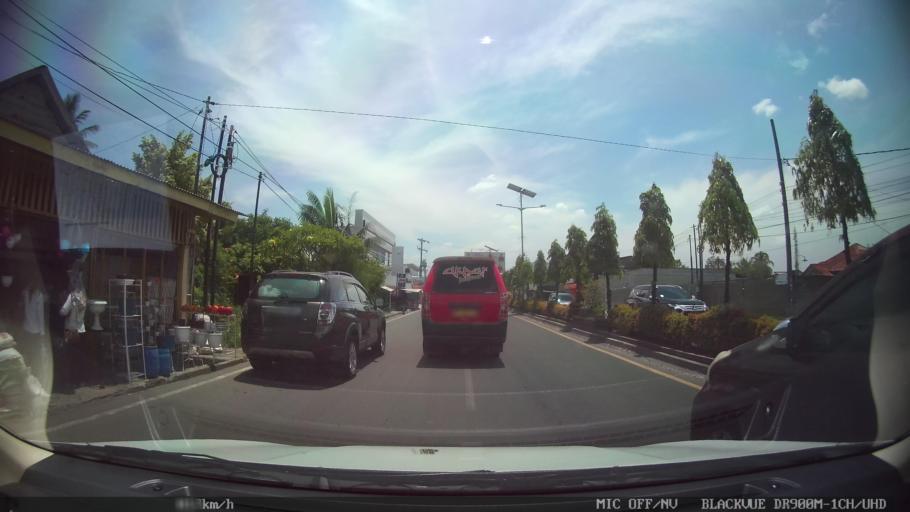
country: ID
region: North Sumatra
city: Binjai
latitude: 3.6085
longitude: 98.4991
